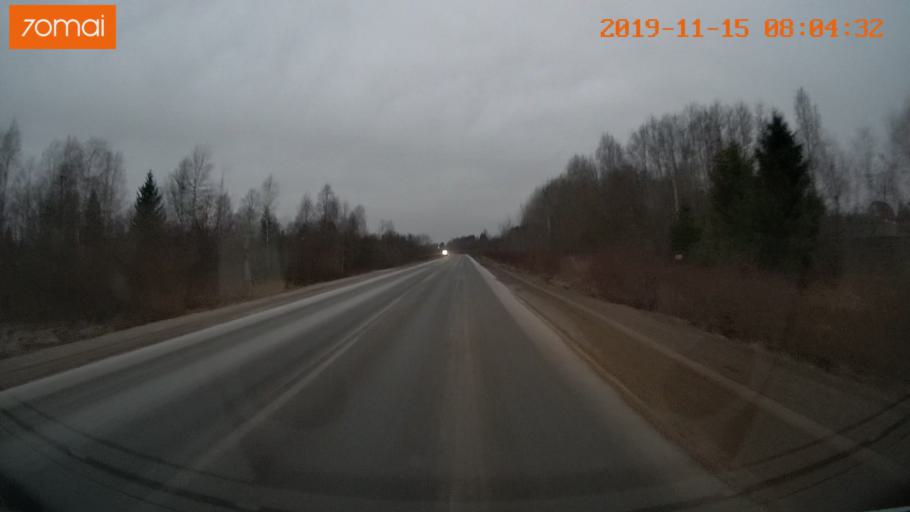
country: RU
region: Vologda
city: Cherepovets
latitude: 59.0092
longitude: 38.0745
